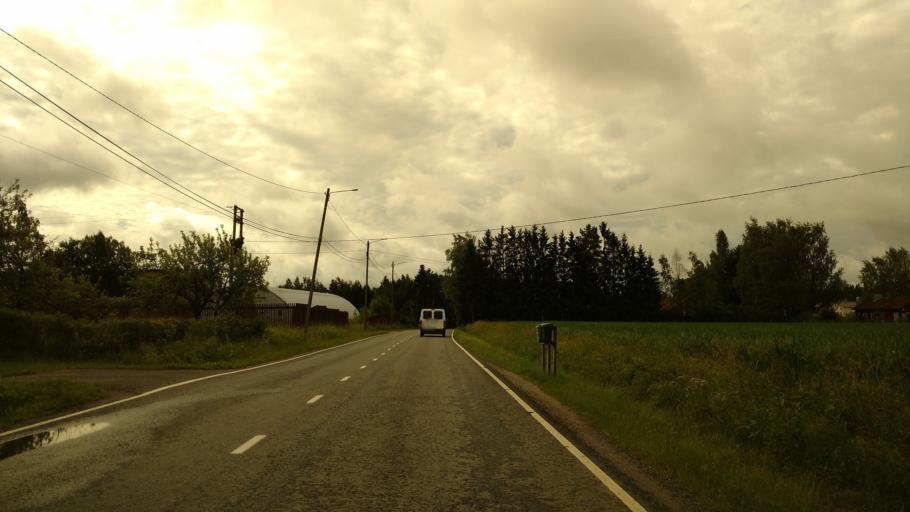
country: FI
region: Varsinais-Suomi
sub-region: Salo
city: Kuusjoki
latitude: 60.5390
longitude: 23.1673
